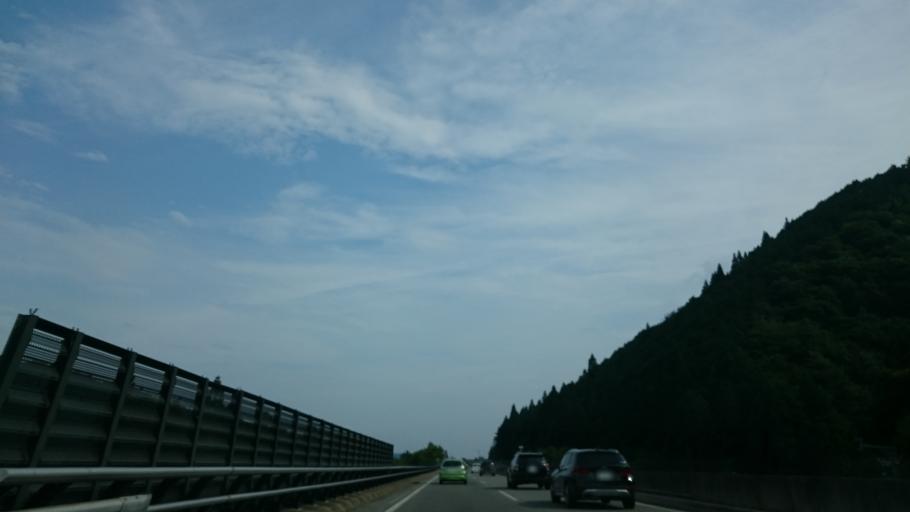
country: JP
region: Gifu
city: Gujo
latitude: 35.8416
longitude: 136.8757
